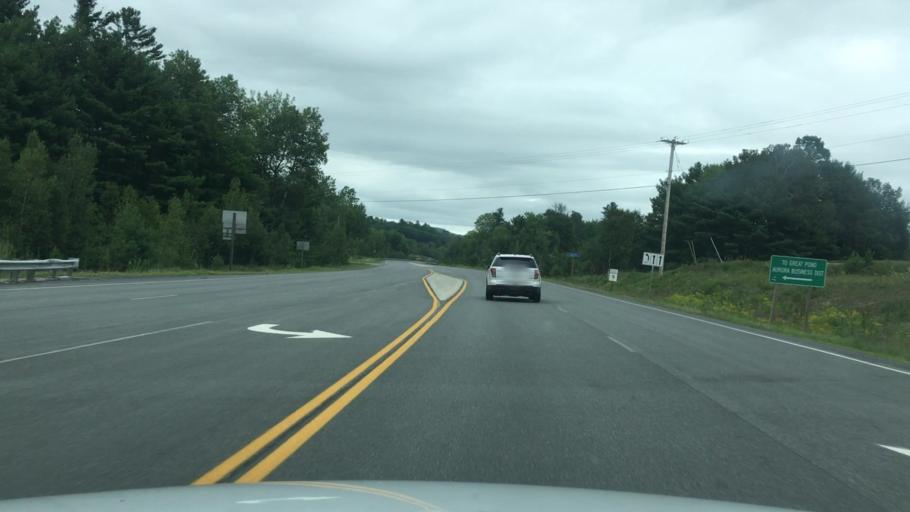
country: US
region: Maine
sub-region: Hancock County
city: Franklin
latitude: 44.8505
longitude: -68.3305
